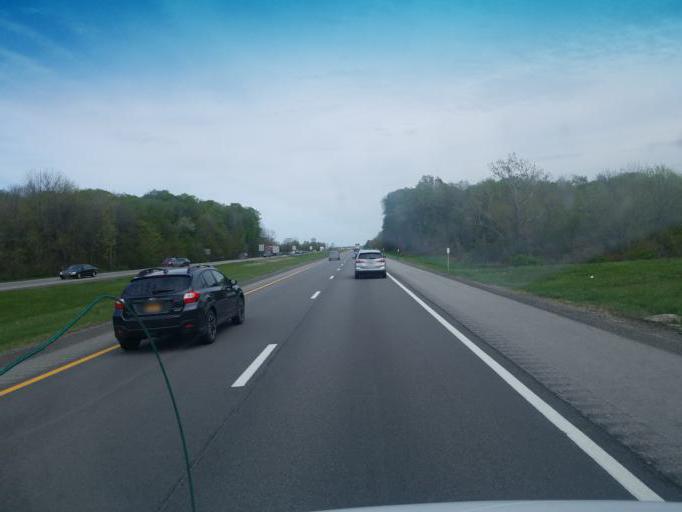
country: US
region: New York
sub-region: Genesee County
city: Le Roy
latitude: 43.0287
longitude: -77.9860
